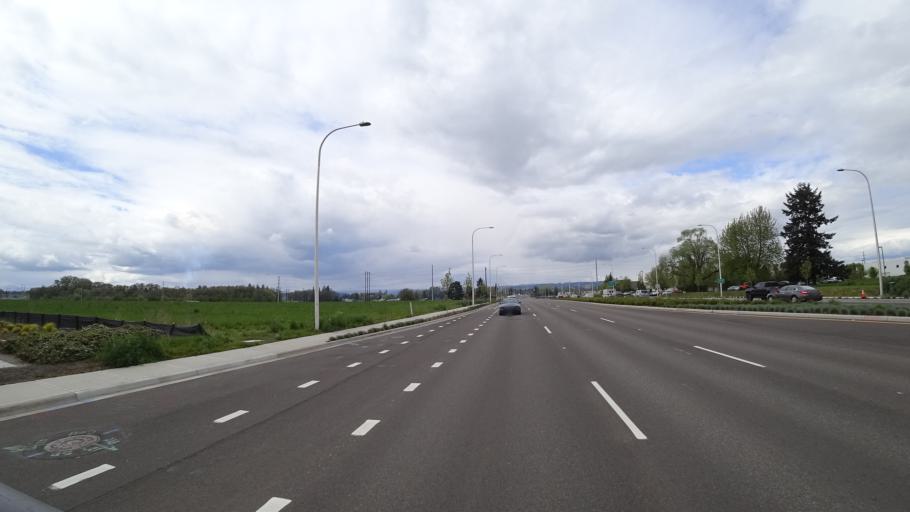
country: US
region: Oregon
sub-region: Washington County
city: Rockcreek
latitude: 45.5545
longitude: -122.9265
